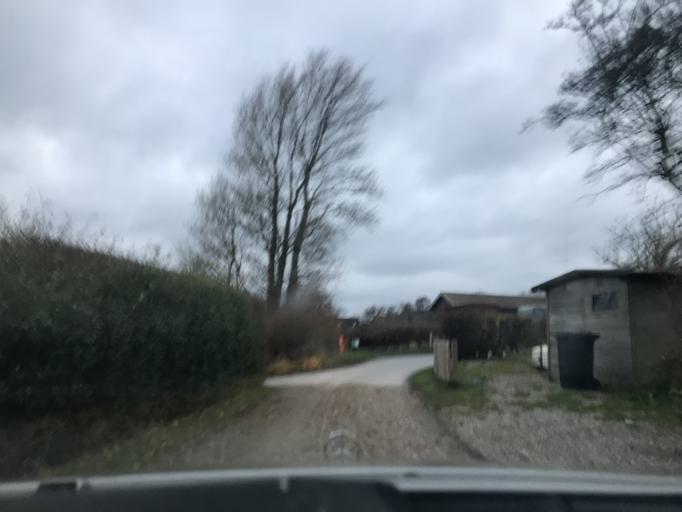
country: DK
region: South Denmark
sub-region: Sonderborg Kommune
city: Horuphav
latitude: 54.8611
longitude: 9.9197
